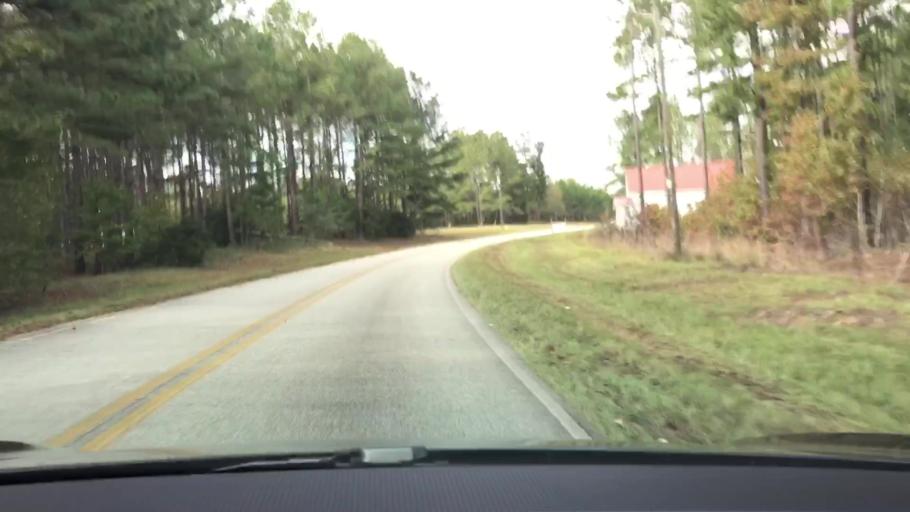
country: US
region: Georgia
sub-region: Jefferson County
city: Wadley
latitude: 32.7990
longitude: -82.3783
